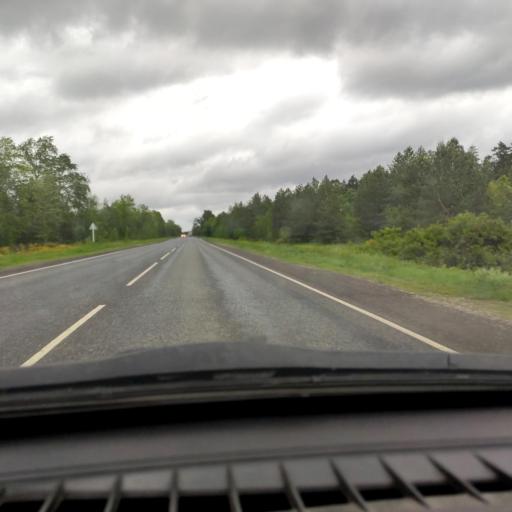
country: RU
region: Samara
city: Povolzhskiy
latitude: 53.6175
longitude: 49.6330
